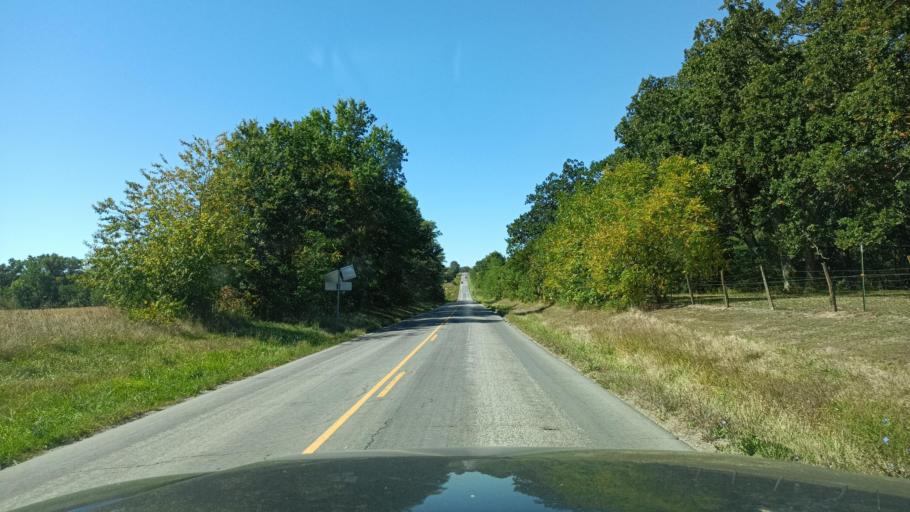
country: US
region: Missouri
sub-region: Macon County
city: La Plata
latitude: 40.0233
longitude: -92.5885
